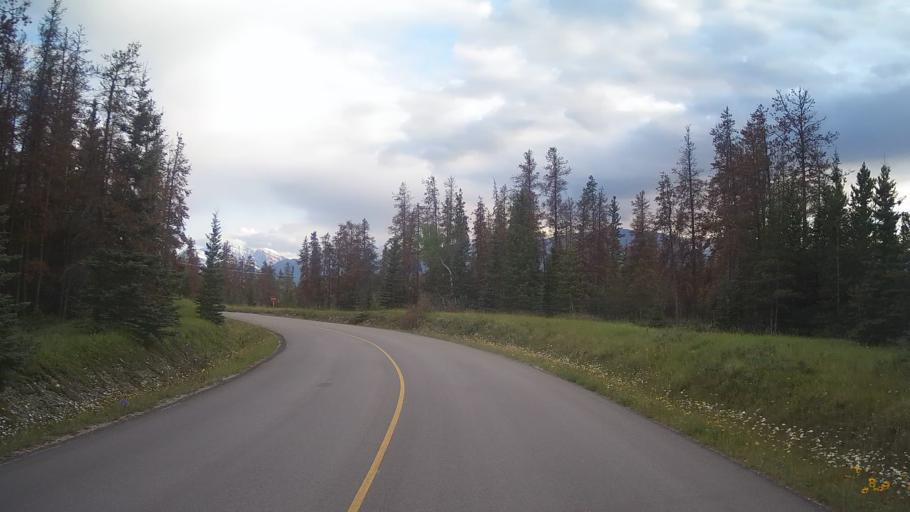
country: CA
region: Alberta
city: Jasper Park Lodge
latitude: 52.9235
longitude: -118.0361
